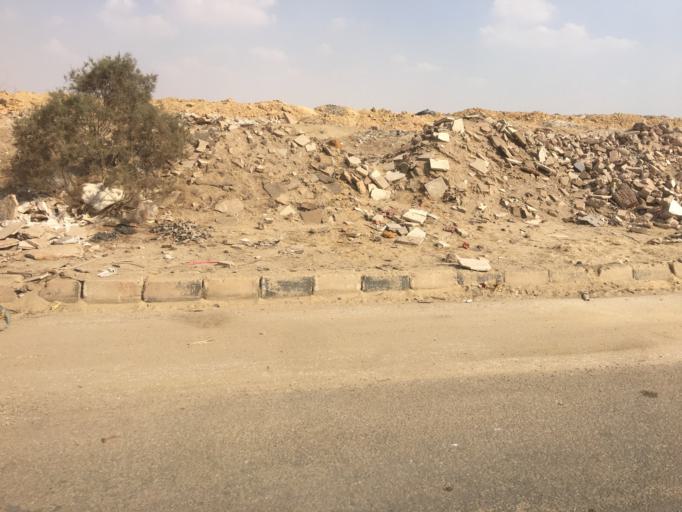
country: EG
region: Eastern Province
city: Bilbays
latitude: 30.2589
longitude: 31.7675
